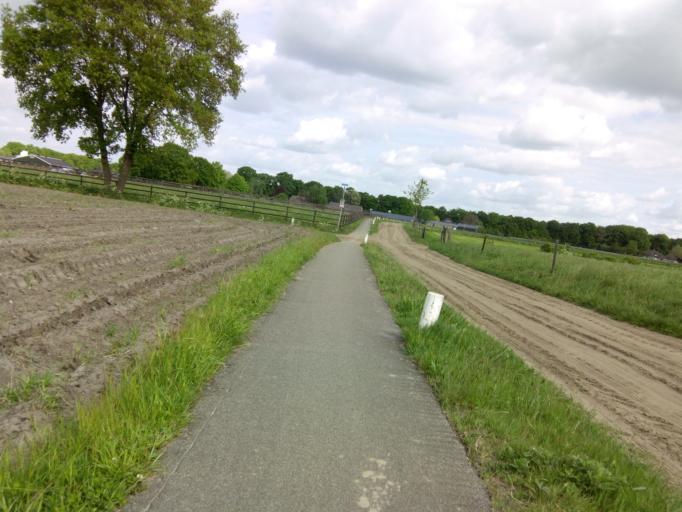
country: NL
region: Gelderland
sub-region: Gemeente Ede
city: Lunteren
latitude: 52.0697
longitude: 5.6444
